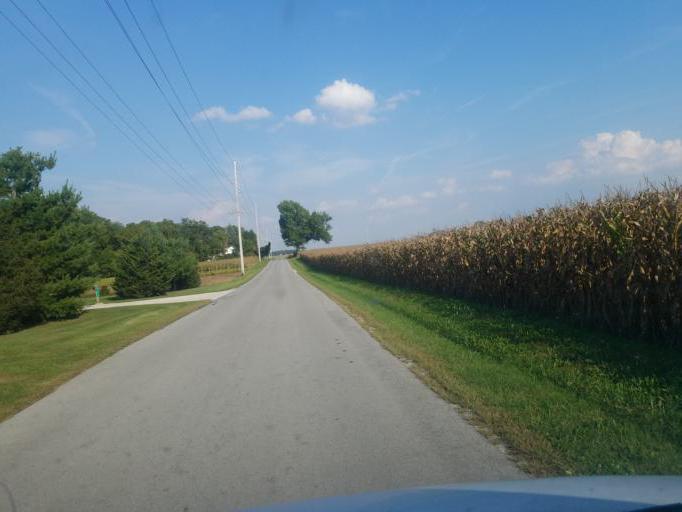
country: US
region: Ohio
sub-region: Wyandot County
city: Carey
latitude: 40.9237
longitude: -83.3094
